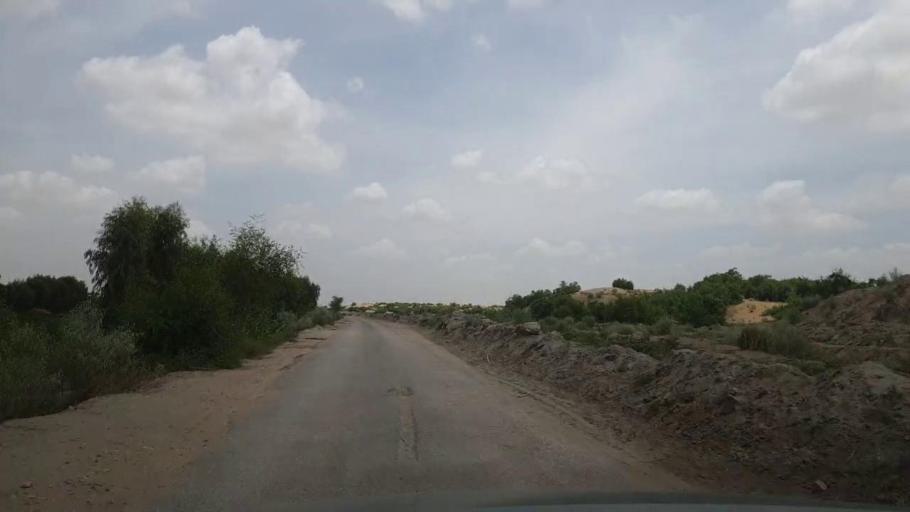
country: PK
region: Sindh
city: Kot Diji
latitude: 27.1981
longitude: 69.0722
